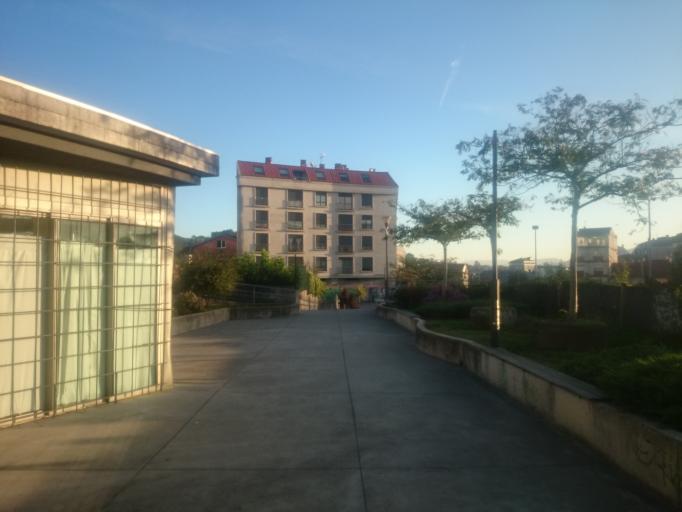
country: ES
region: Galicia
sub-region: Provincia de Pontevedra
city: Porrino
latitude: 42.1599
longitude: -8.6186
